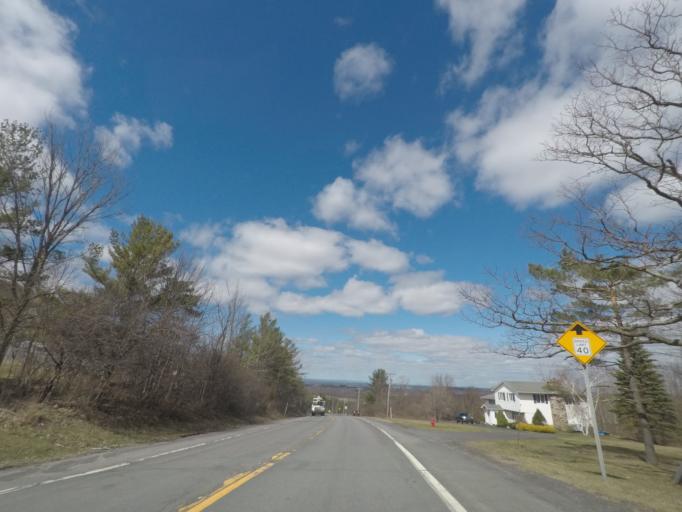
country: US
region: New York
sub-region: Albany County
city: Voorheesville
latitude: 42.6199
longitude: -73.9755
